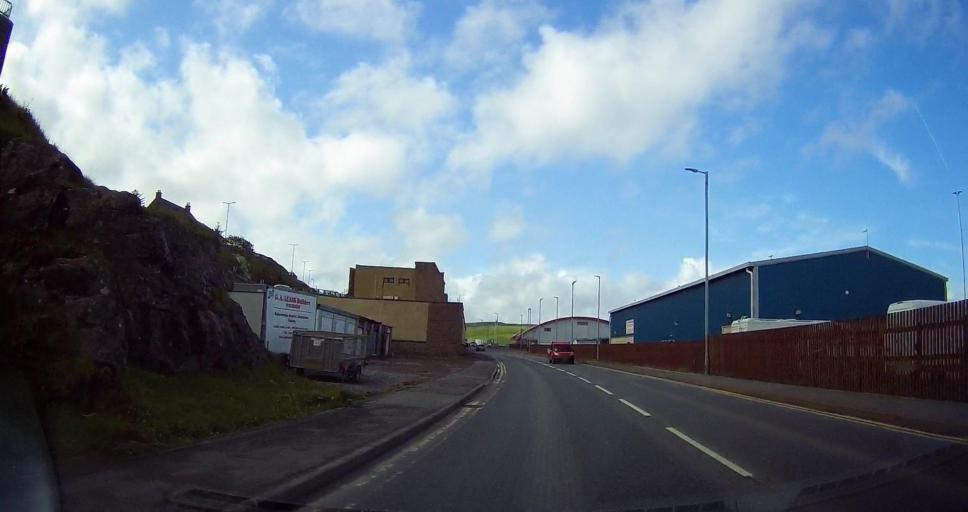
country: GB
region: Scotland
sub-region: Shetland Islands
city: Lerwick
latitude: 60.1606
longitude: -1.1577
